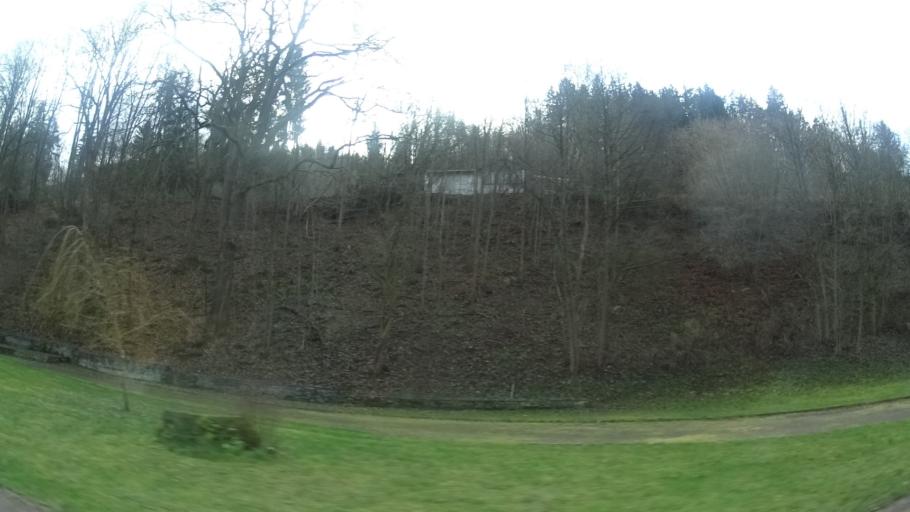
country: DE
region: Thuringia
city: Sitzendorf
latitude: 50.6314
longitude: 11.1754
